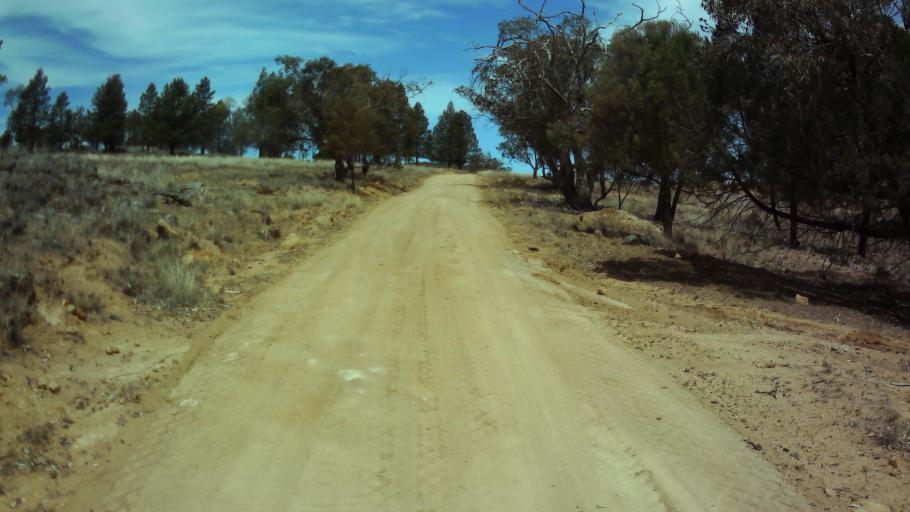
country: AU
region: New South Wales
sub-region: Weddin
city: Grenfell
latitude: -33.7880
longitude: 148.1562
